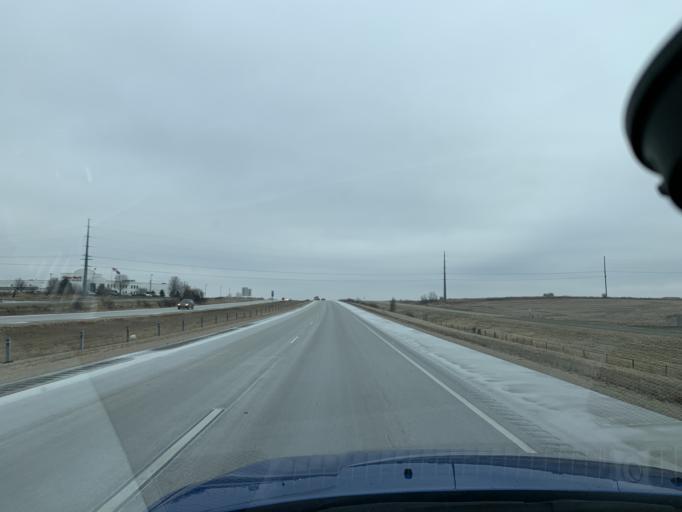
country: US
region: Wisconsin
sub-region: Dane County
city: Sun Prairie
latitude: 43.2016
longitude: -89.1949
